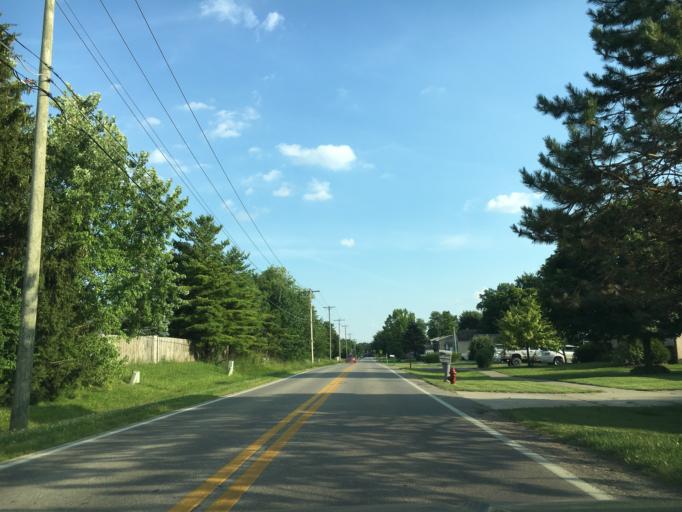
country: US
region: Ohio
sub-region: Franklin County
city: Hilliard
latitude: 39.9878
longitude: -83.1653
